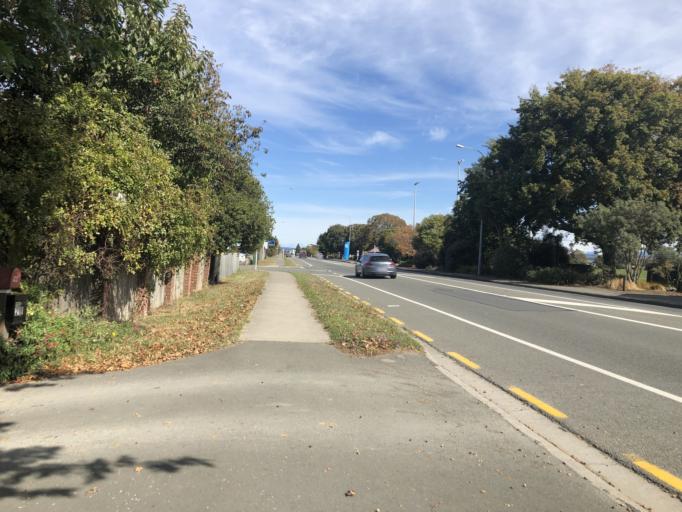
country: NZ
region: Tasman
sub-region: Tasman District
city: Richmond
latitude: -41.3387
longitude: 173.1786
